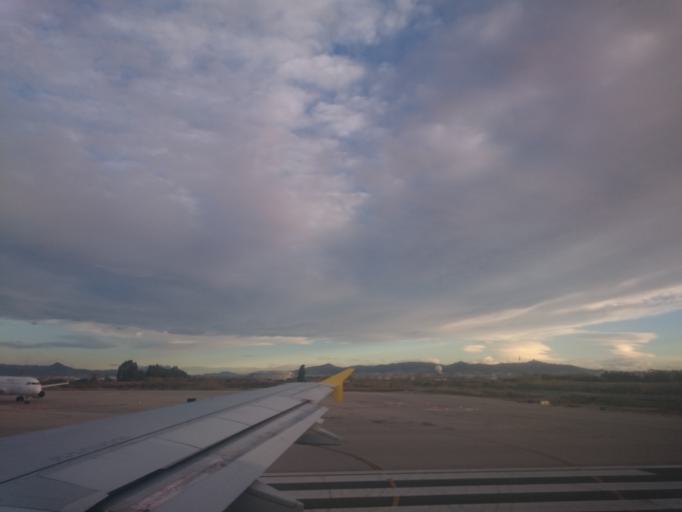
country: ES
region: Catalonia
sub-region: Provincia de Barcelona
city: El Prat de Llobregat
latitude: 41.2921
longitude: 2.1030
